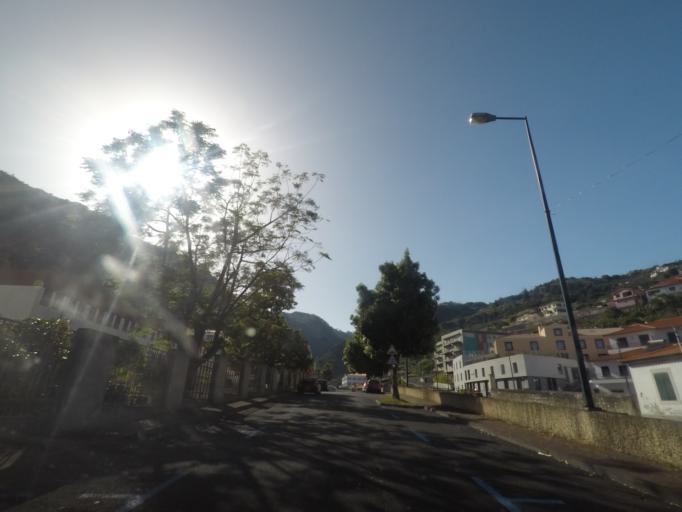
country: PT
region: Madeira
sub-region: Santa Cruz
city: Santa Cruz
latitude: 32.6889
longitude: -16.7950
